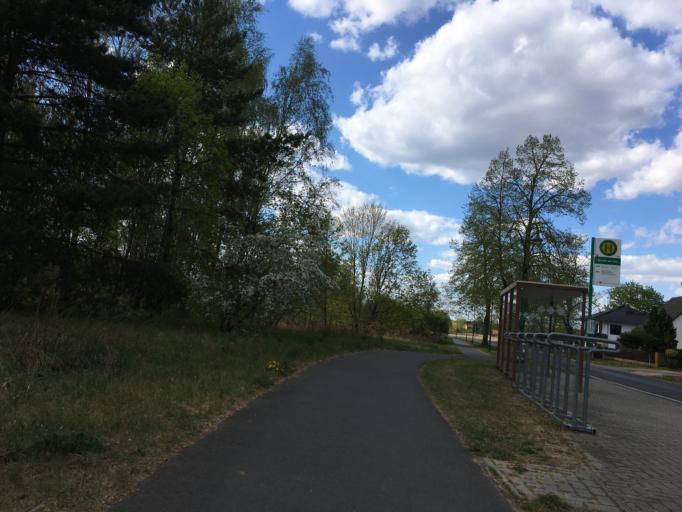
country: DE
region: Brandenburg
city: Wandlitz
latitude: 52.7759
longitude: 13.4463
